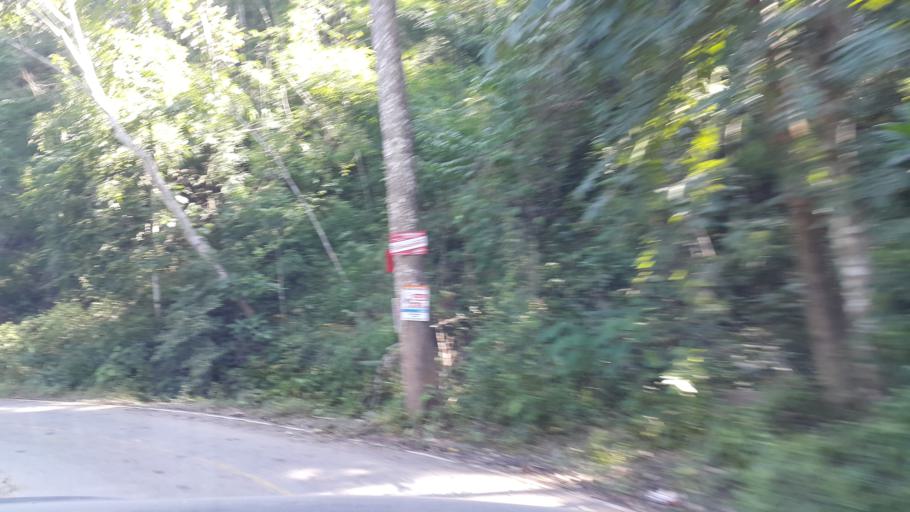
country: TH
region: Chiang Mai
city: Samoeng
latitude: 18.8705
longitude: 98.6249
